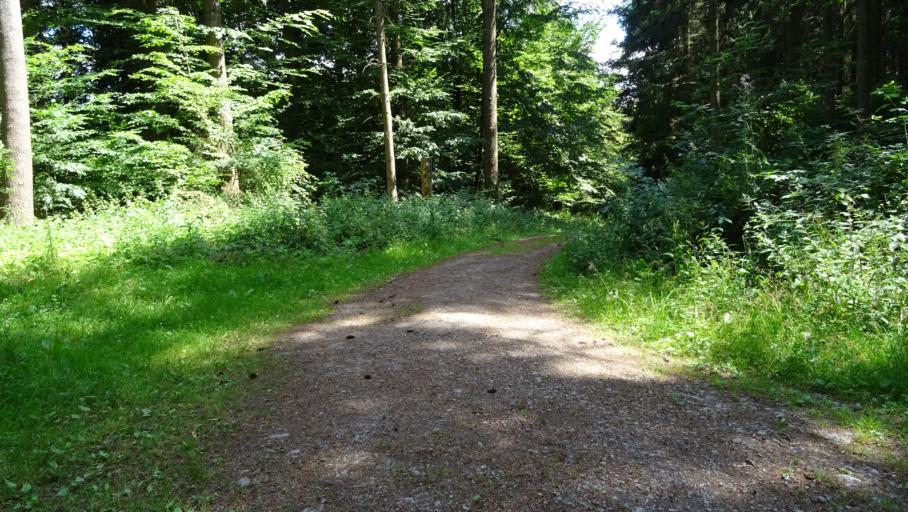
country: DE
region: Baden-Wuerttemberg
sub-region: Karlsruhe Region
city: Neckargerach
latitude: 49.3829
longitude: 9.0879
